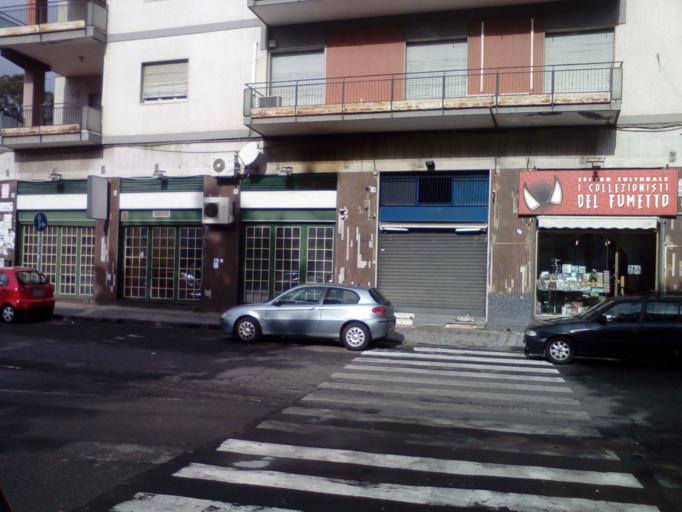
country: IT
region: Sicily
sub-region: Catania
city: Catania
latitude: 37.5160
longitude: 15.0803
